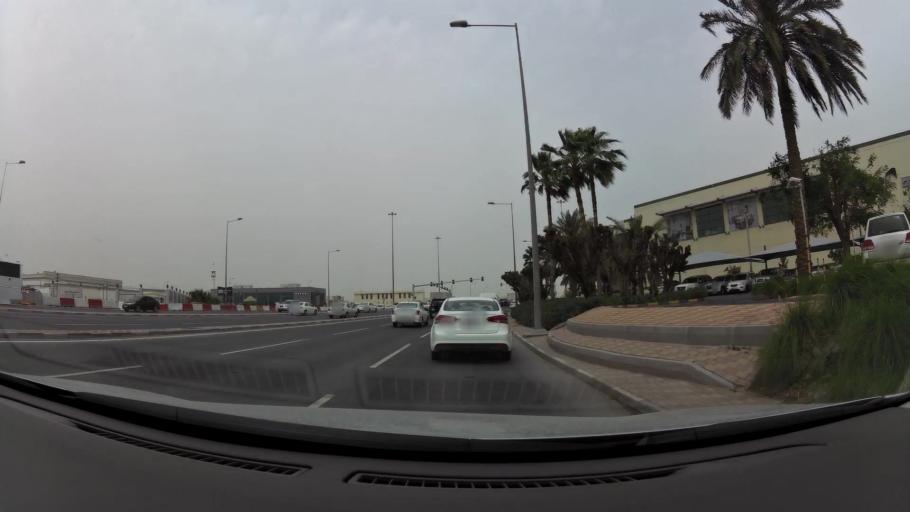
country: QA
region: Baladiyat ad Dawhah
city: Doha
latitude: 25.2529
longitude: 51.5366
